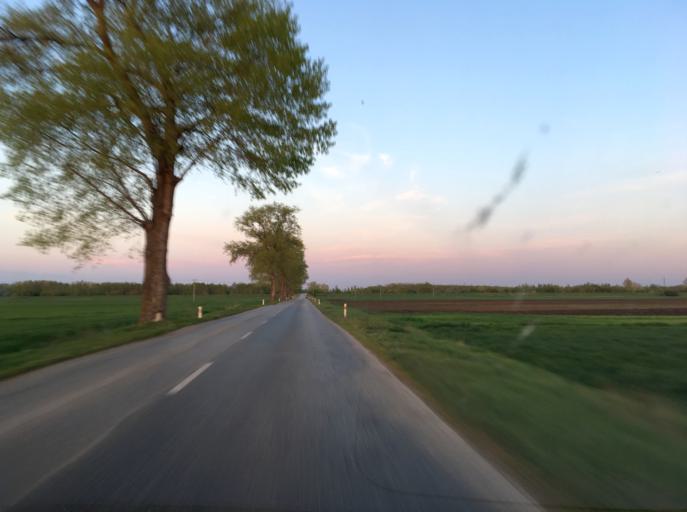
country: SK
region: Nitriansky
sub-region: Okres Nove Zamky
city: Nove Zamky
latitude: 47.9224
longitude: 18.0981
